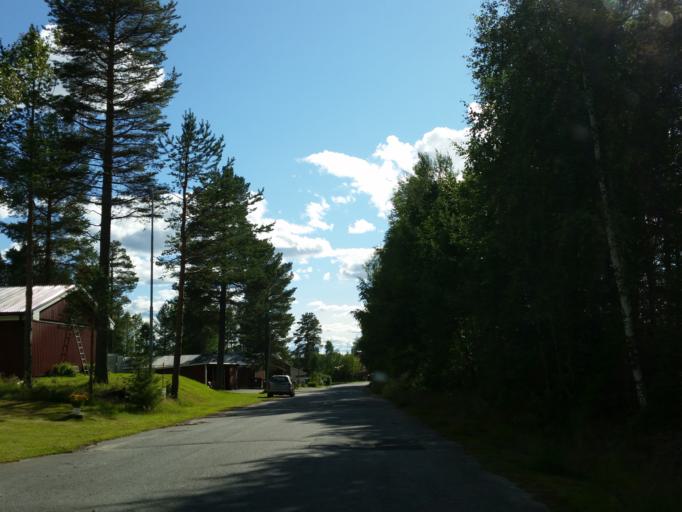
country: SE
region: Vaesterbotten
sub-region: Robertsfors Kommun
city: Robertsfors
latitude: 64.1979
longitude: 20.8508
